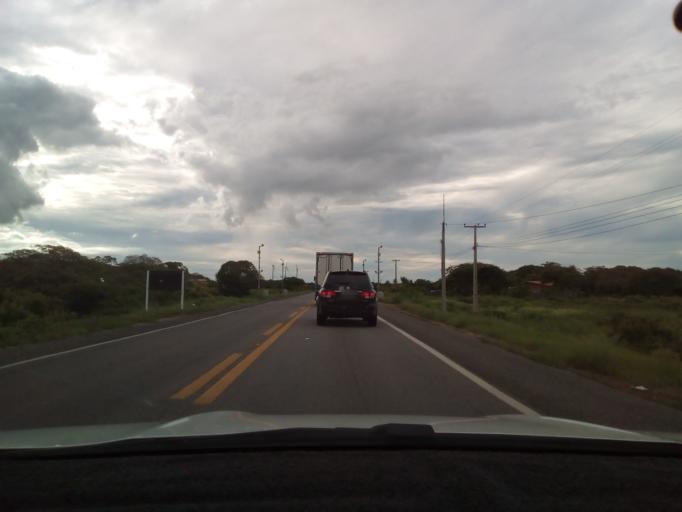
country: BR
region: Ceara
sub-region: Aracati
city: Aracati
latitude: -4.6165
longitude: -37.6536
